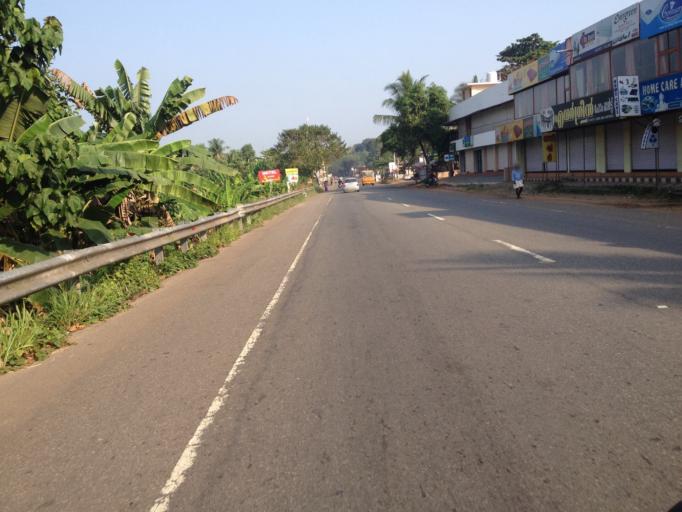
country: IN
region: Kerala
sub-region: Pattanamtitta
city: Adur
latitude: 9.0946
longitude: 76.7529
